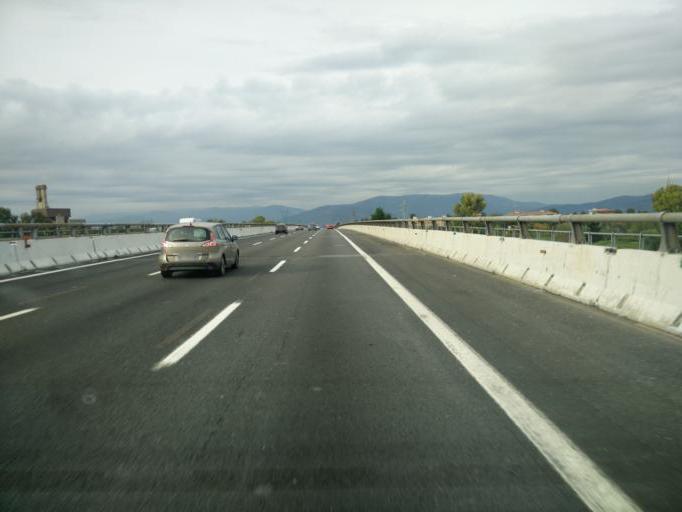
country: IT
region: Tuscany
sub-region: Province of Florence
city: Mantignano-Ugnano
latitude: 43.7857
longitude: 11.1592
